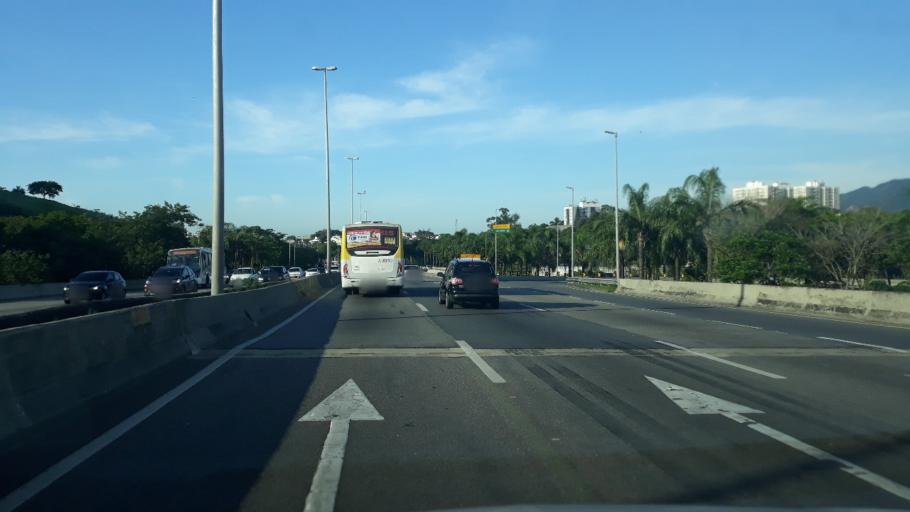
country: BR
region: Rio de Janeiro
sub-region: Sao Joao De Meriti
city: Sao Joao de Meriti
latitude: -22.9386
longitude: -43.3496
